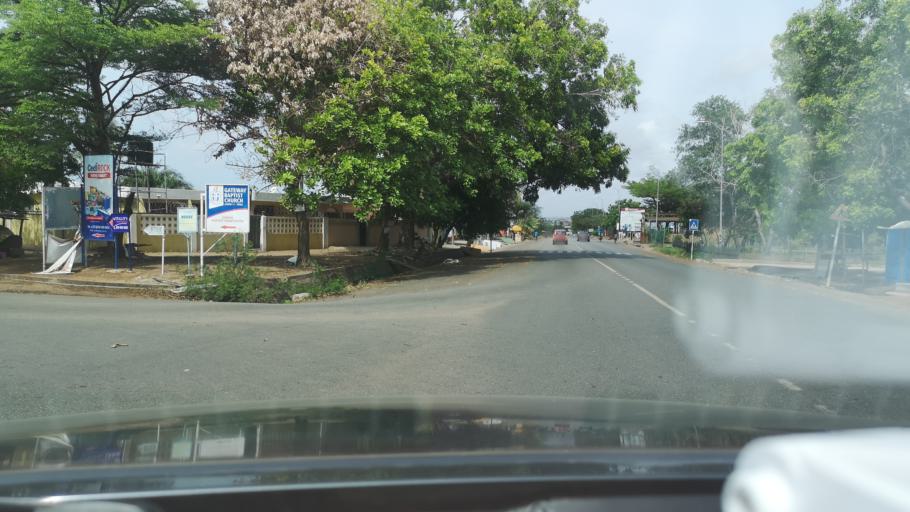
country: GH
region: Greater Accra
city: Tema
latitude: 5.6673
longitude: -0.0292
